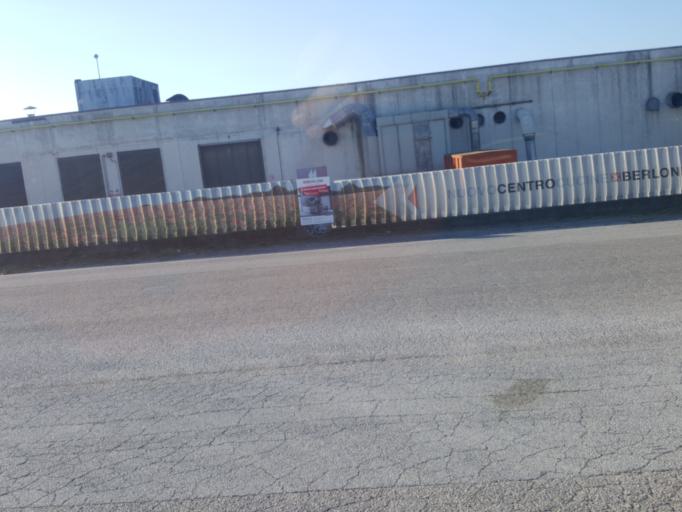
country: IT
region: The Marches
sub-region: Provincia di Pesaro e Urbino
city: Borgo Santa Maria
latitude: 43.8633
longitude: 12.8137
